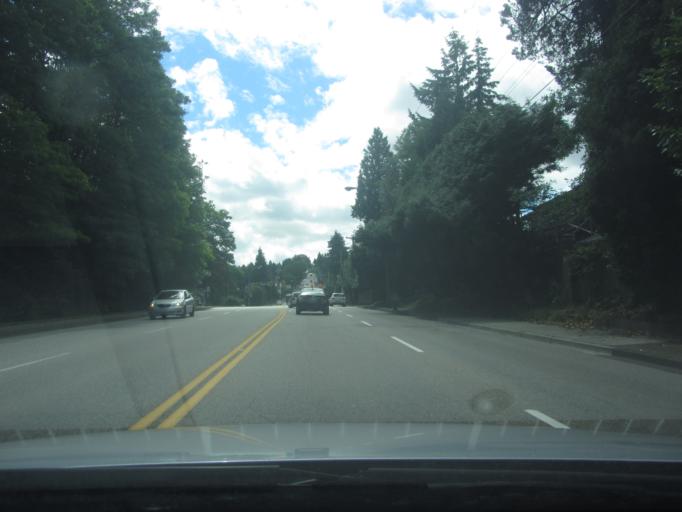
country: CA
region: British Columbia
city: Burnaby
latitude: 49.2368
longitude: -122.9560
